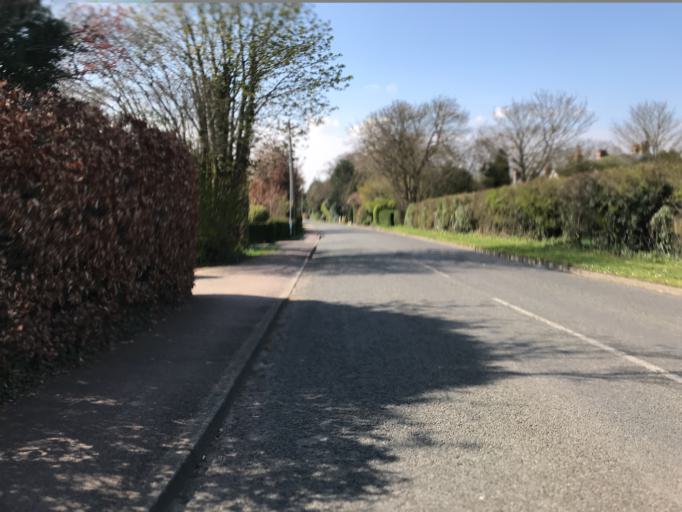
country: GB
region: England
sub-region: Cambridgeshire
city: Sawston
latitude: 52.1549
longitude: 0.1498
